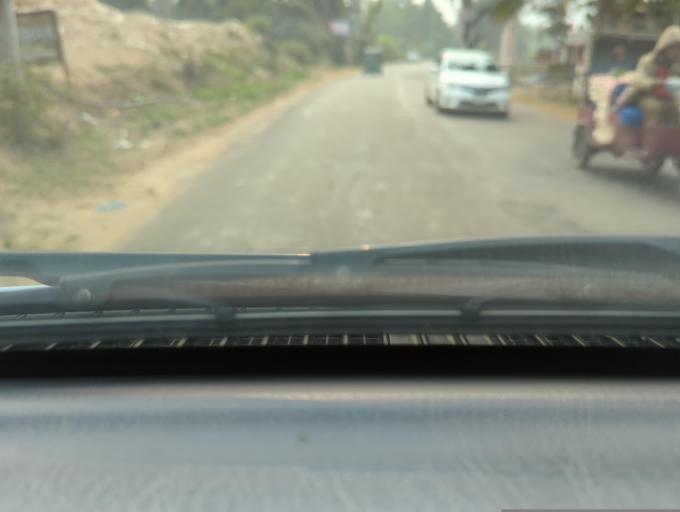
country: BD
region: Sylhet
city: Maulavi Bazar
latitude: 24.5279
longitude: 91.7339
